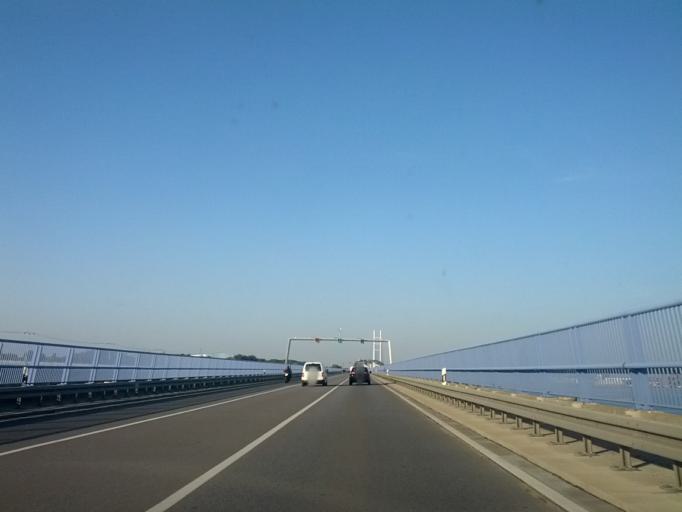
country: DE
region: Mecklenburg-Vorpommern
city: Altefahr
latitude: 54.3182
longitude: 13.1304
